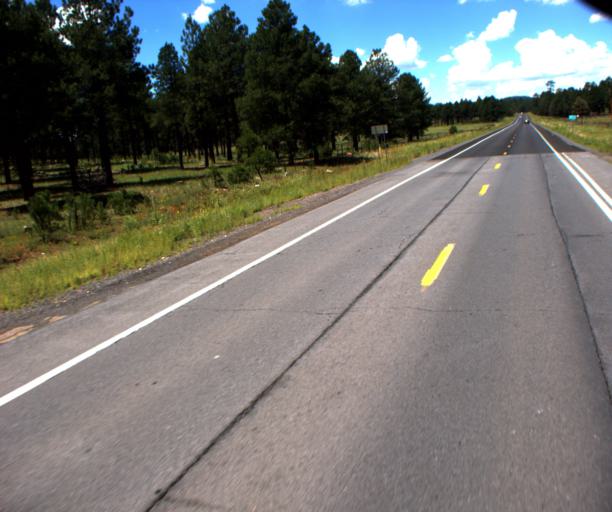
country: US
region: Arizona
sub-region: Coconino County
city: Flagstaff
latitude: 35.1898
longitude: -111.6972
